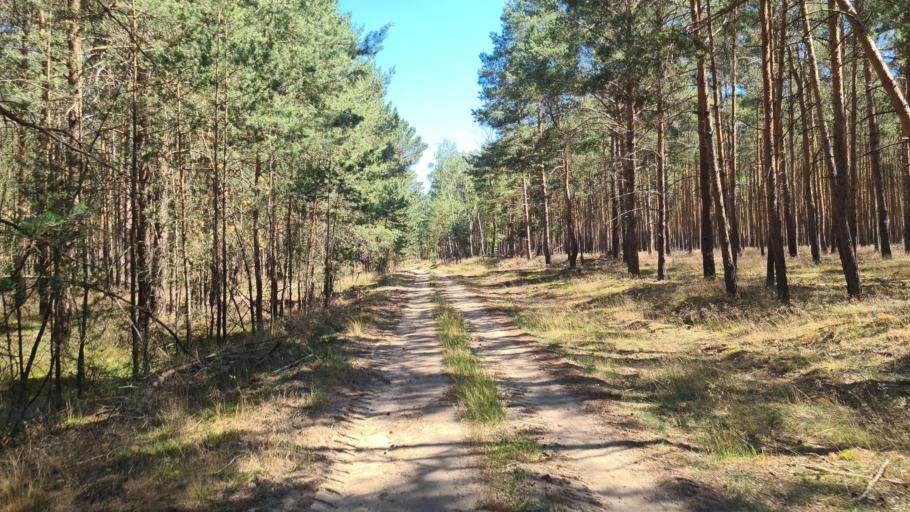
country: DE
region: Brandenburg
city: Treuenbrietzen
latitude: 52.0551
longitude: 12.7988
